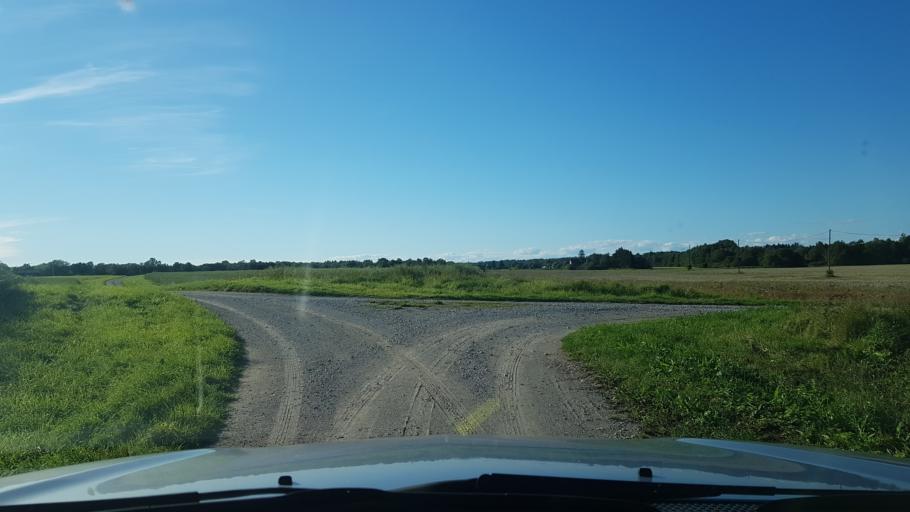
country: EE
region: Harju
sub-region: Rae vald
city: Jueri
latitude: 59.3850
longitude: 24.8802
